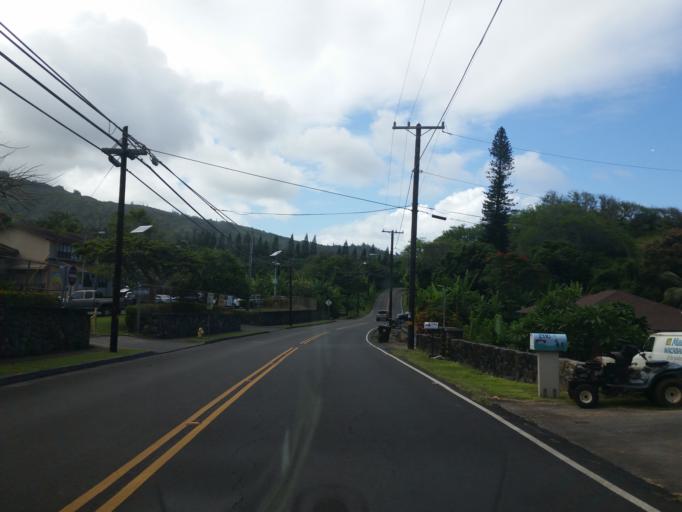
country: US
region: Hawaii
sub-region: Maui County
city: Waihee-Waiehu
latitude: 20.9341
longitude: -156.5130
